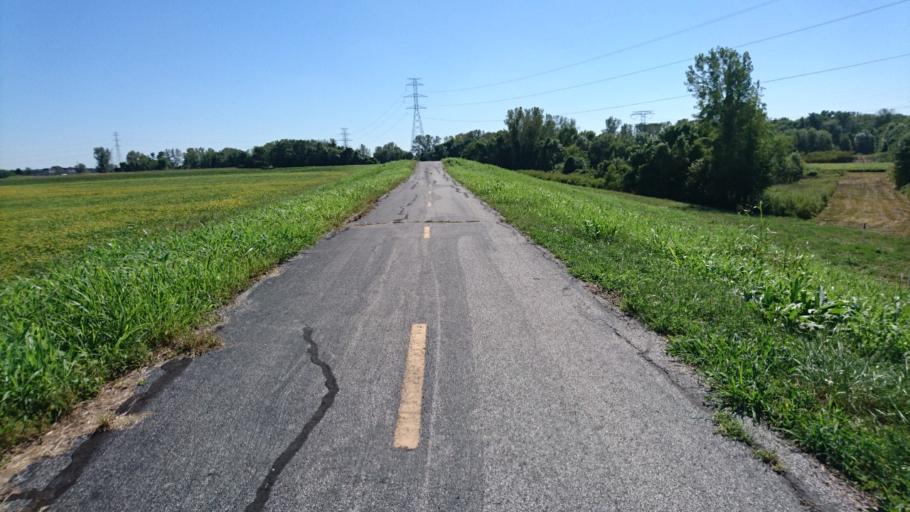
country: US
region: Illinois
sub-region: Madison County
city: Hartford
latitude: 38.8097
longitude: -90.1016
